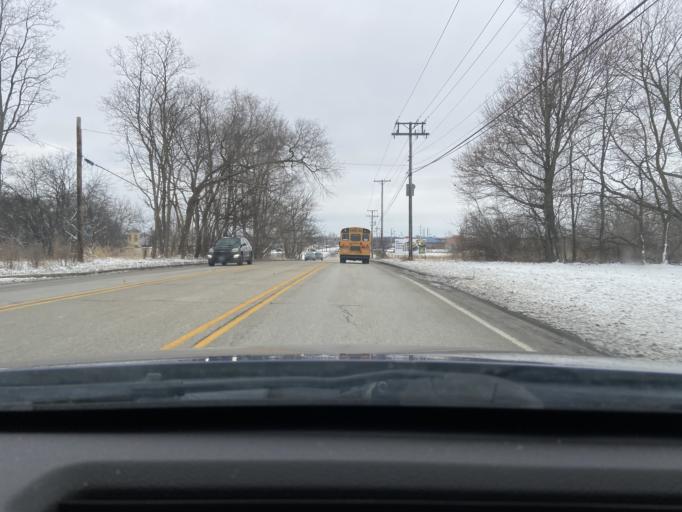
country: US
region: Illinois
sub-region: Lake County
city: Venetian Village
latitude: 42.3897
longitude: -88.0638
